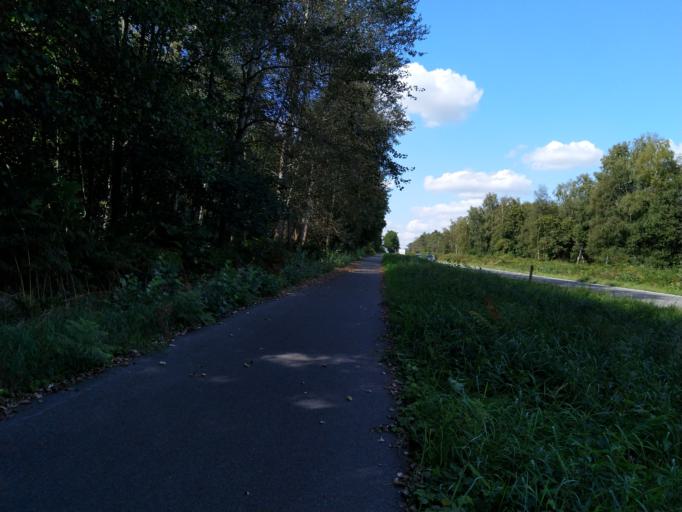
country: BE
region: Wallonia
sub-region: Province du Hainaut
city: Saint-Ghislain
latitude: 50.4862
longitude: 3.8097
